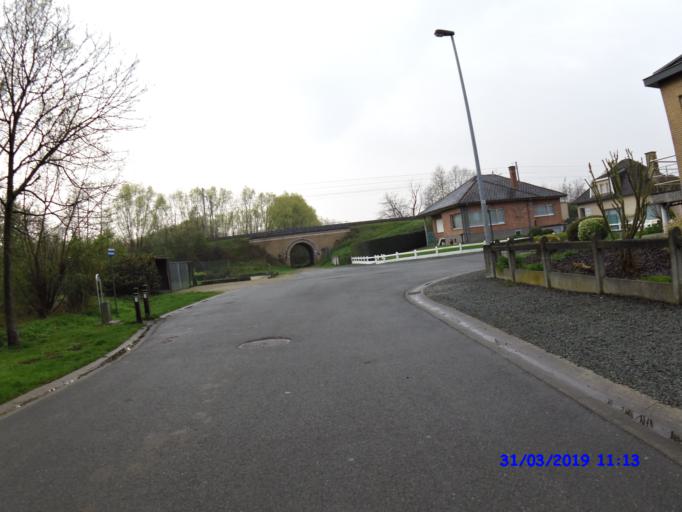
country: BE
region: Flanders
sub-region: Provincie Oost-Vlaanderen
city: Denderleeuw
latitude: 50.8891
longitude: 4.0963
